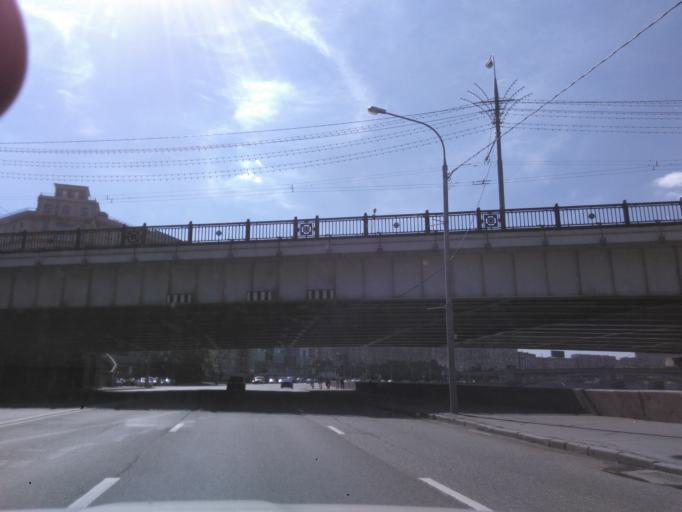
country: RU
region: Moskovskaya
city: Dorogomilovo
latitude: 55.7528
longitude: 37.5730
